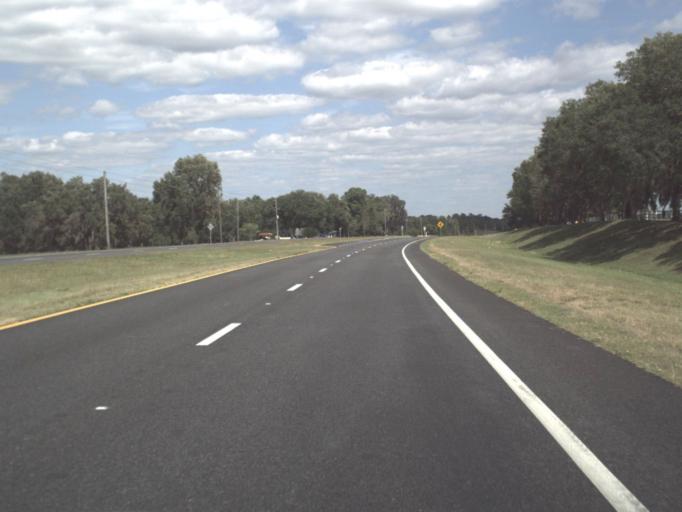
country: US
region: Florida
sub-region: Marion County
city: Ocala
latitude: 29.2309
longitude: -82.2511
